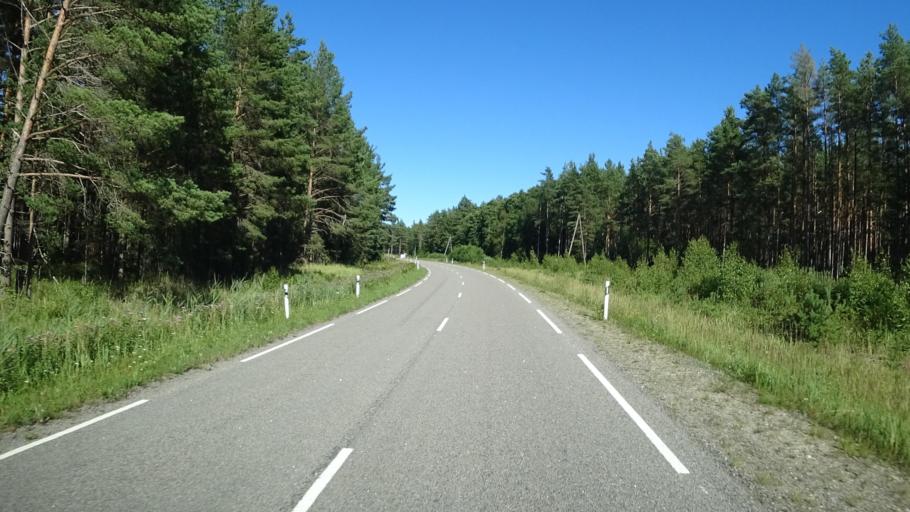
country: LV
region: Dundaga
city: Dundaga
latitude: 57.6771
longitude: 22.3436
